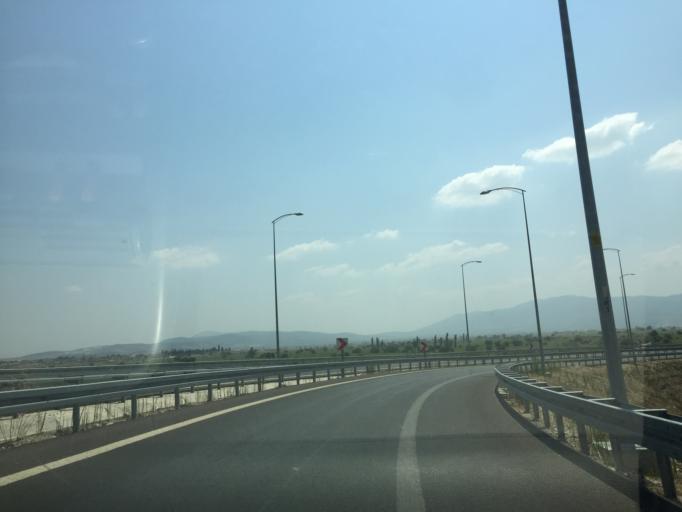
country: TR
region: Manisa
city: Halitpasa
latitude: 38.7668
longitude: 27.6619
